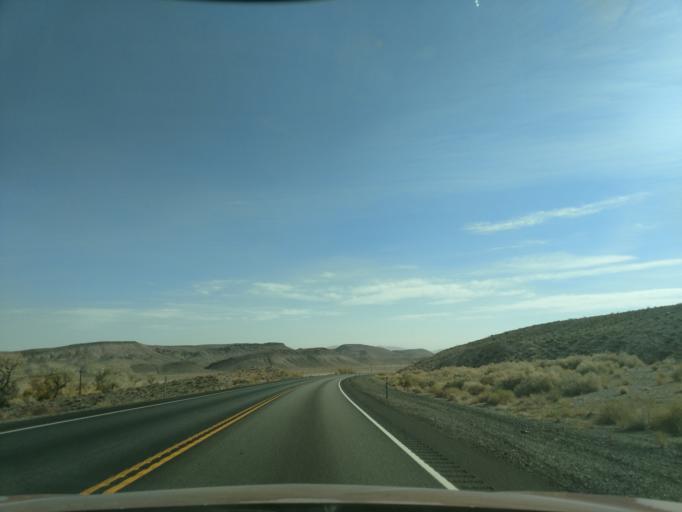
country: US
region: Nevada
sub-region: Nye County
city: Beatty
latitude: 37.0195
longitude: -116.7362
